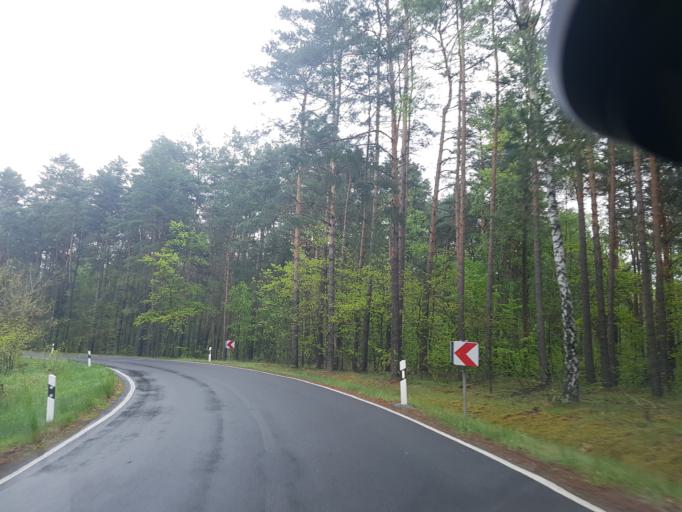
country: DE
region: Brandenburg
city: Spremberg
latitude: 51.6324
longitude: 14.4323
